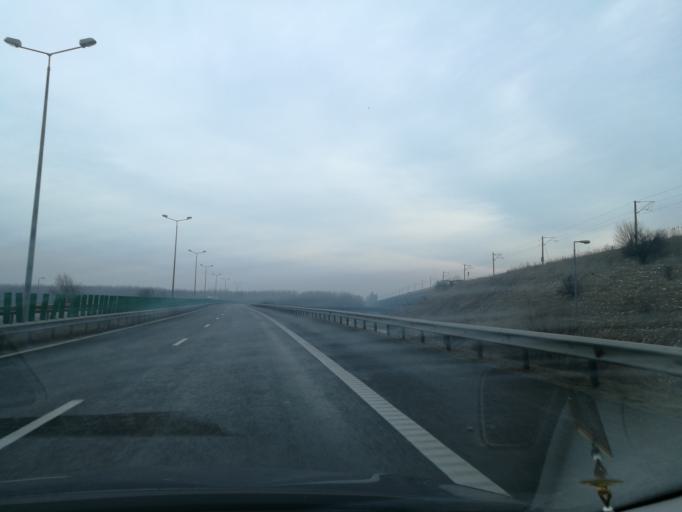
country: RO
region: Constanta
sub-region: Oras Cernavoda
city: Cernavoda
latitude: 44.3457
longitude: 27.9976
